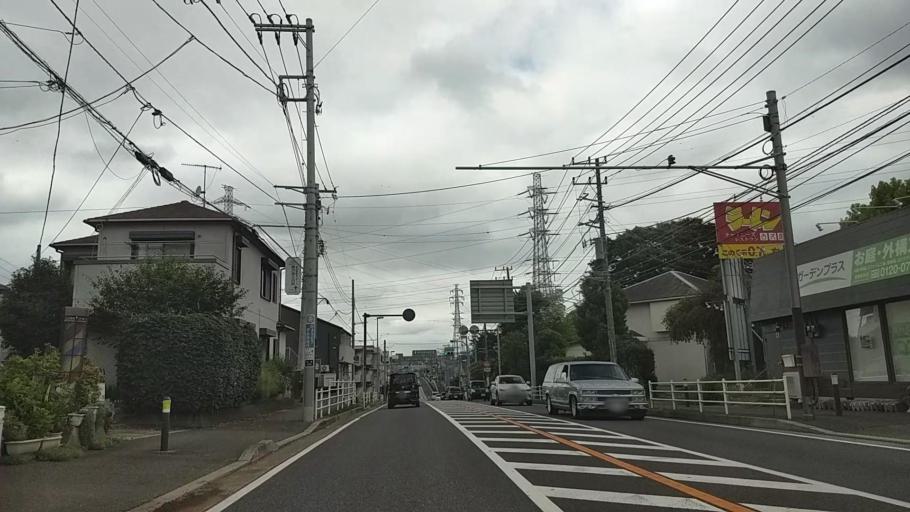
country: JP
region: Kanagawa
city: Fujisawa
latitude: 35.4105
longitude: 139.4698
